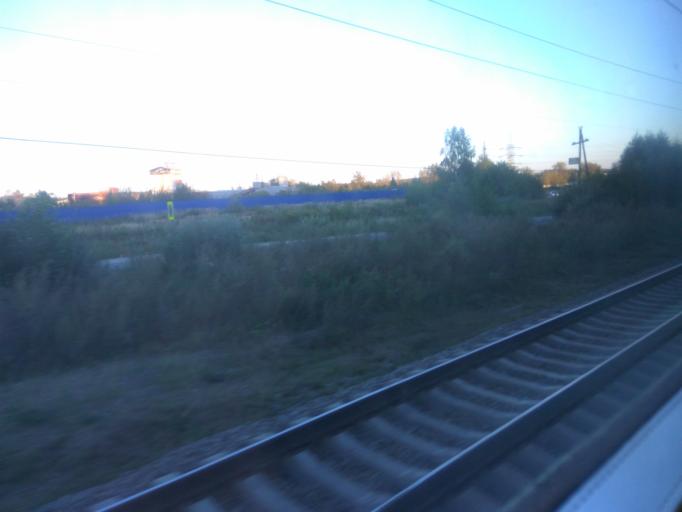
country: RU
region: Moskovskaya
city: Elektrostal'
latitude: 55.7794
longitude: 38.4641
